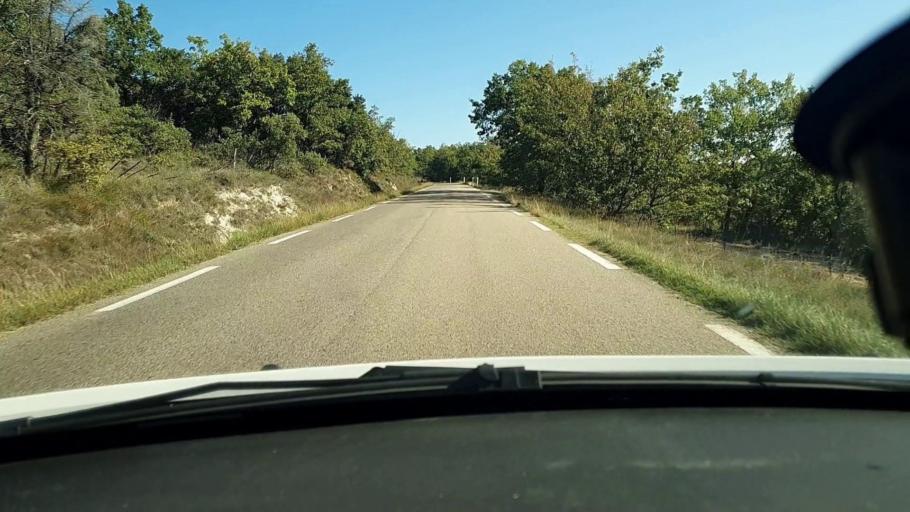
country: FR
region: Languedoc-Roussillon
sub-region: Departement du Gard
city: Goudargues
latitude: 44.2854
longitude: 4.4644
